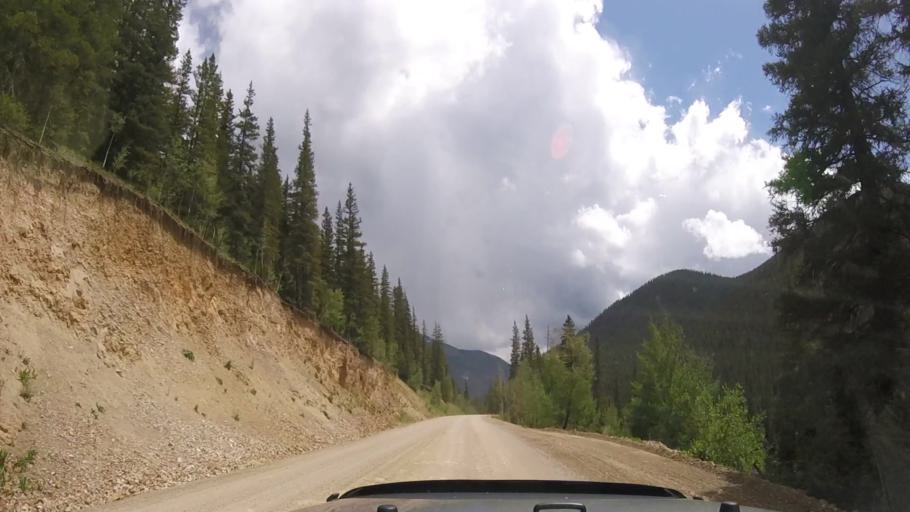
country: US
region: Colorado
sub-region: San Juan County
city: Silverton
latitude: 37.8333
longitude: -107.6719
